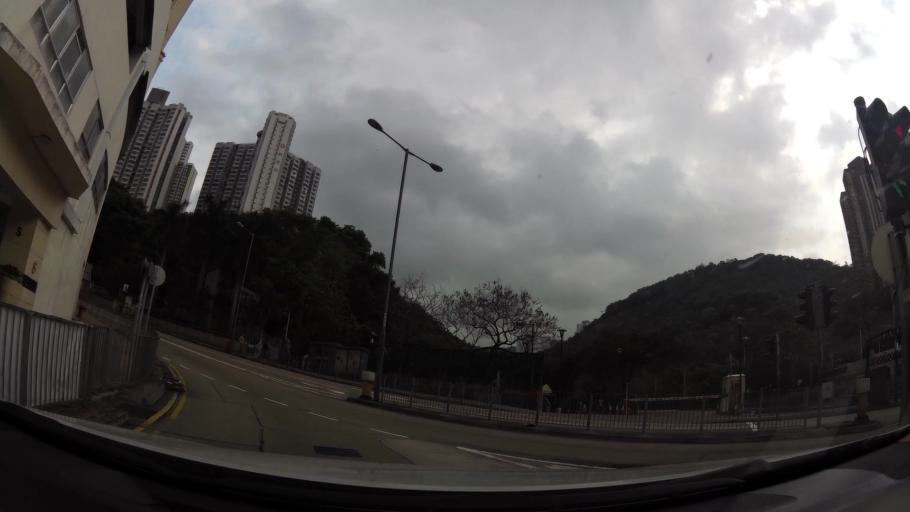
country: HK
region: Kowloon City
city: Kowloon
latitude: 22.3240
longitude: 114.2175
